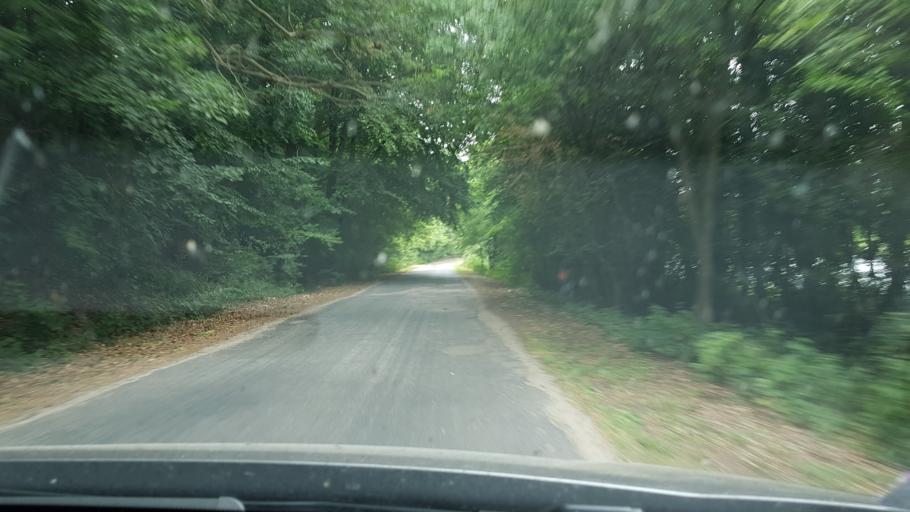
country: PL
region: West Pomeranian Voivodeship
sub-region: Powiat kamienski
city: Miedzyzdroje
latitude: 53.9588
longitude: 14.5689
